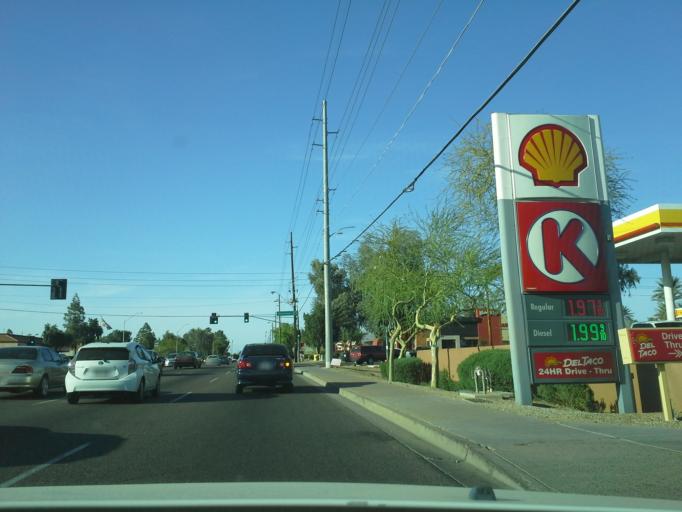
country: US
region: Arizona
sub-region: Maricopa County
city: Glendale
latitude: 33.6245
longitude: -112.1336
